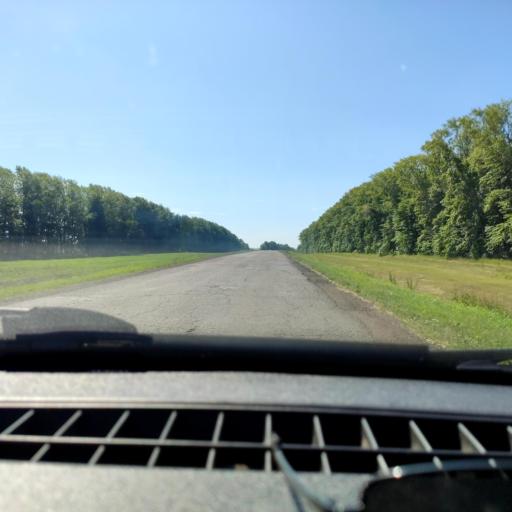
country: RU
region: Bashkortostan
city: Karmaskaly
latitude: 54.3910
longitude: 56.1736
